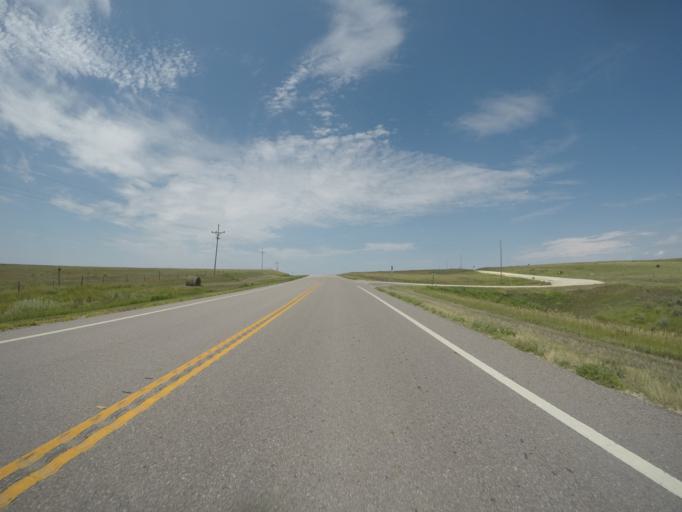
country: US
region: Kansas
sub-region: Rooks County
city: Stockton
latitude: 39.4517
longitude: -99.1407
